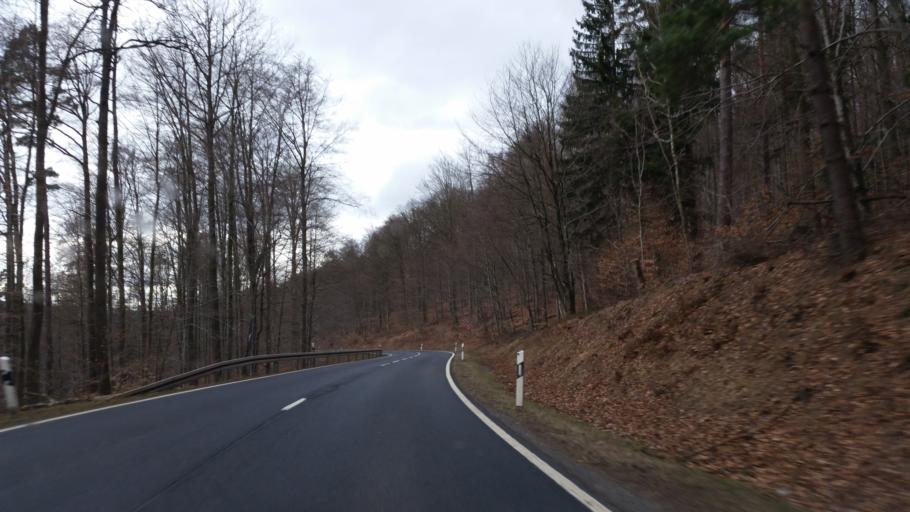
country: DE
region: Bavaria
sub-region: Regierungsbezirk Unterfranken
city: Heigenbrucken
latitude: 49.9968
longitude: 9.3698
